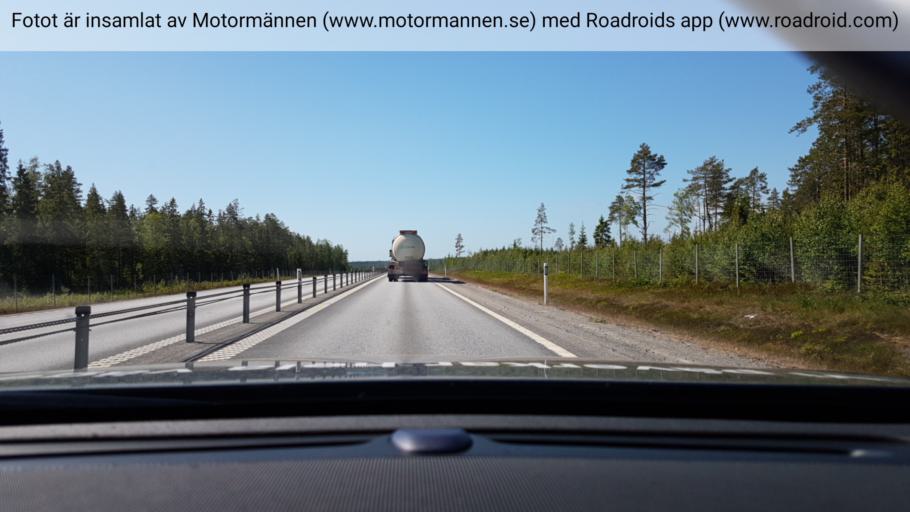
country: SE
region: Vaesterbotten
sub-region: Umea Kommun
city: Hoernefors
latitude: 63.7070
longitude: 20.0490
